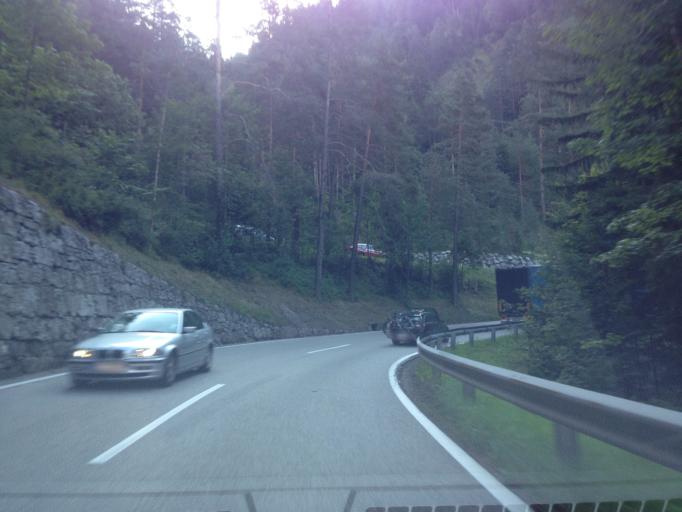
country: AT
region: Tyrol
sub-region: Politischer Bezirk Imst
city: Nassereith
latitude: 47.3532
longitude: 10.8410
